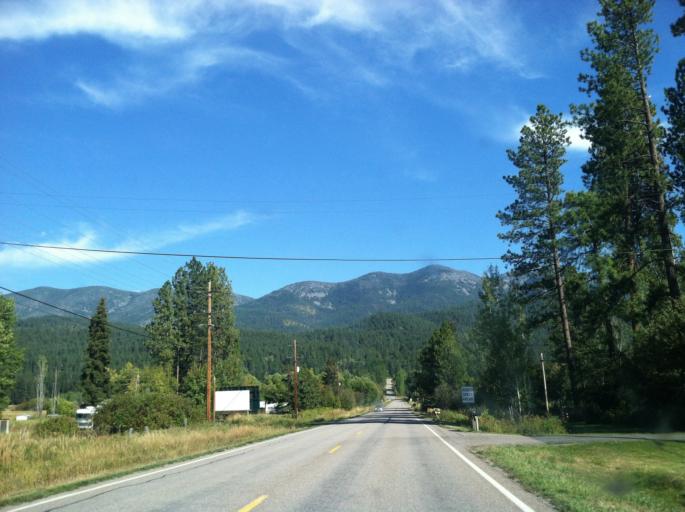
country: US
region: Montana
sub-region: Lake County
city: Polson
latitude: 47.6889
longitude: -114.0641
